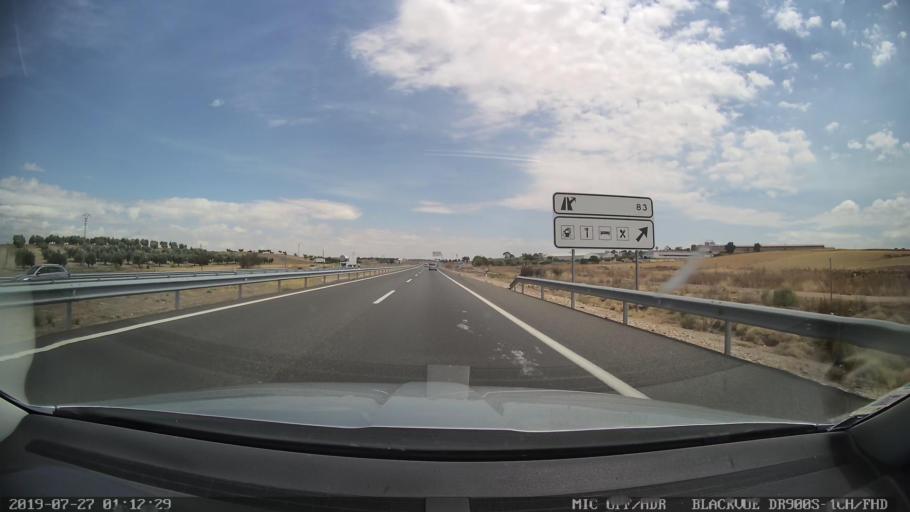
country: ES
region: Castille-La Mancha
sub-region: Province of Toledo
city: Santa Olalla
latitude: 40.0241
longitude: -4.4631
